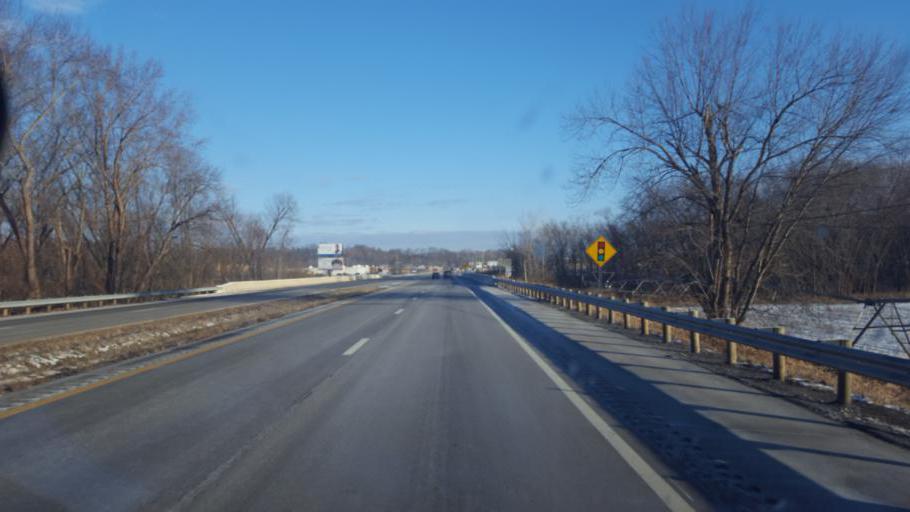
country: US
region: Ohio
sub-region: Pike County
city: Waverly
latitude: 39.1060
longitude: -82.9982
